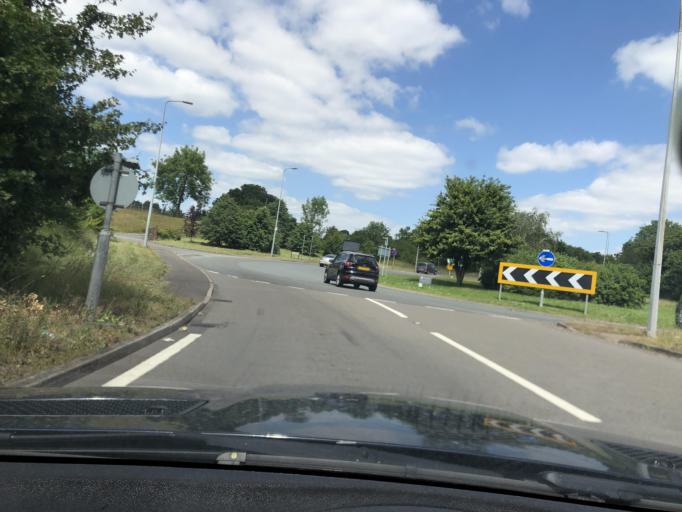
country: GB
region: England
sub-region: Essex
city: Writtle
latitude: 51.6951
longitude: 0.4245
